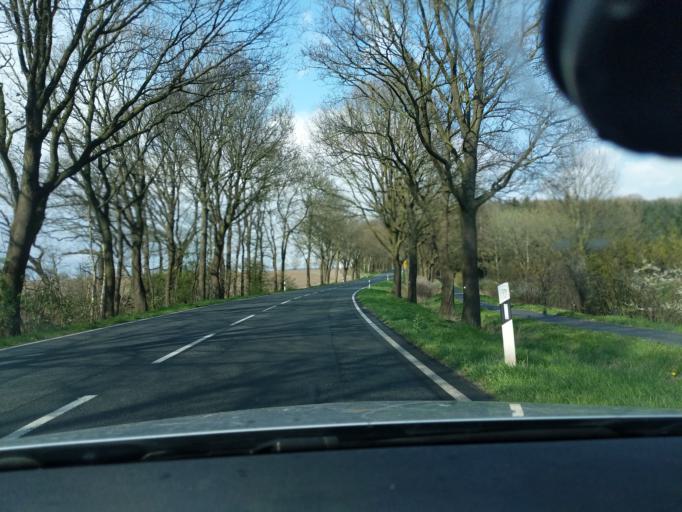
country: DE
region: Lower Saxony
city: Harsefeld
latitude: 53.4707
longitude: 9.4936
